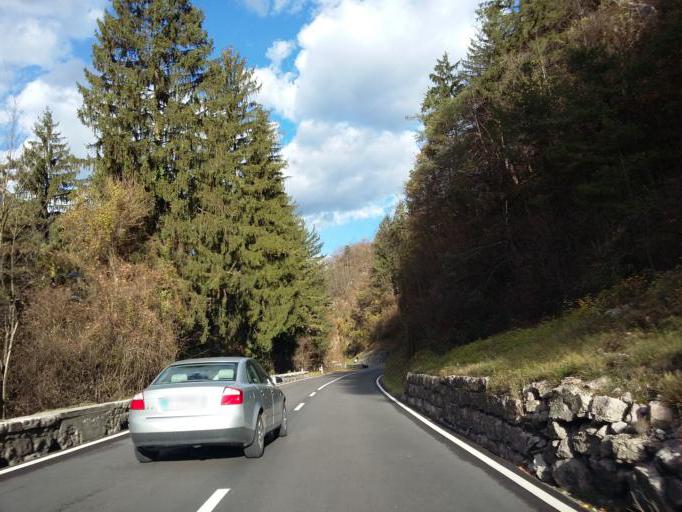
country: IT
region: Trentino-Alto Adige
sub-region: Provincia di Trento
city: Dorsino
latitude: 46.0498
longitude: 10.9009
